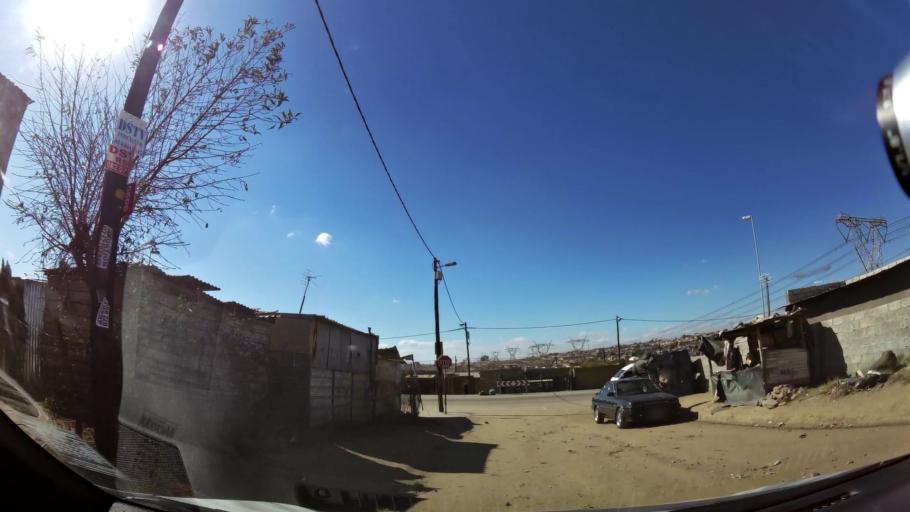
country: ZA
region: Gauteng
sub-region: City of Johannesburg Metropolitan Municipality
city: Midrand
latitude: -25.9197
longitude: 28.0940
